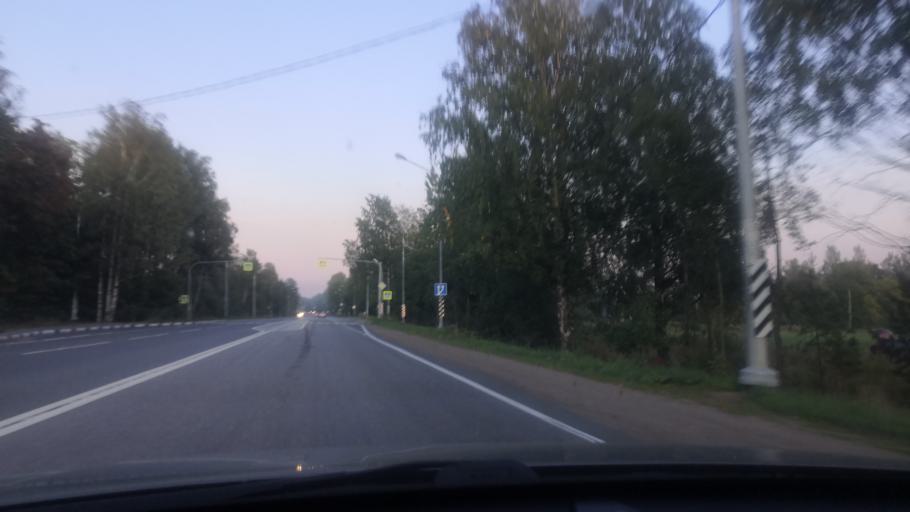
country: RU
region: St.-Petersburg
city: Beloostrov
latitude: 60.1962
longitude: 30.0467
